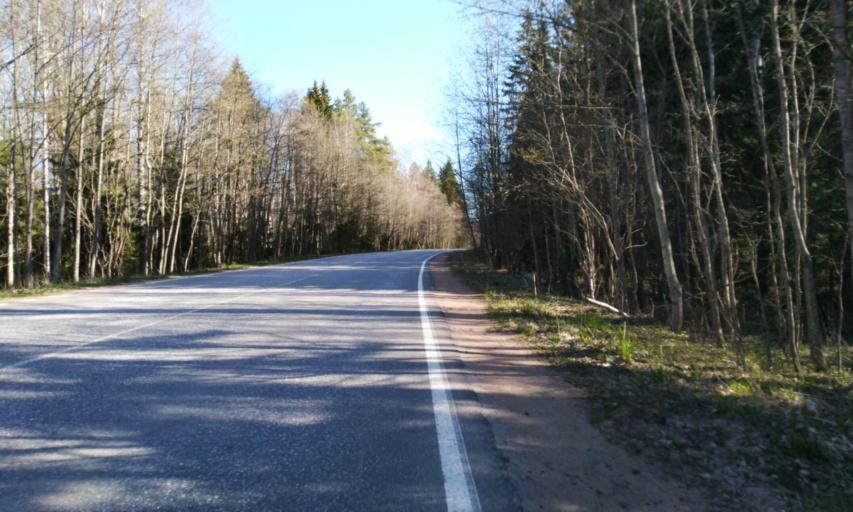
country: RU
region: Leningrad
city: Garbolovo
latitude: 60.3447
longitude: 30.4384
